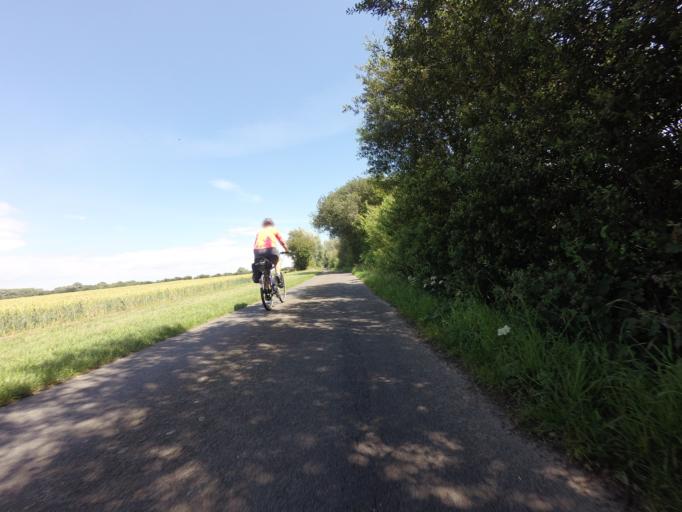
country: GB
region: England
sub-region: Kent
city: Lydd
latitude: 50.9816
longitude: 0.8649
